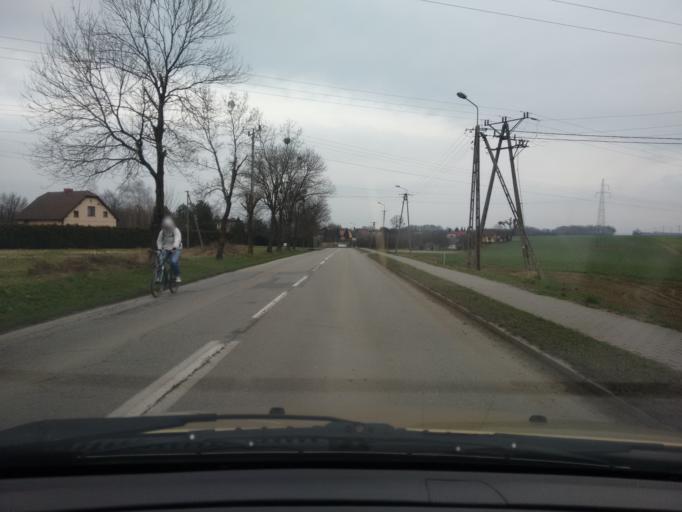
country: PL
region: Silesian Voivodeship
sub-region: Powiat pszczynski
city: Pawlowice
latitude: 49.9613
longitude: 18.7273
